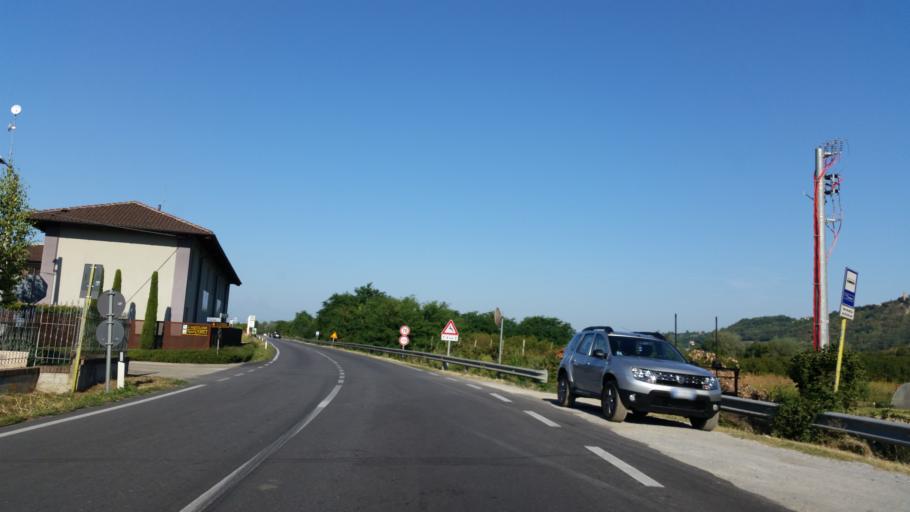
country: IT
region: Piedmont
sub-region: Provincia di Cuneo
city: Santa Vittoria d'Alba
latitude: 44.6835
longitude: 7.9470
